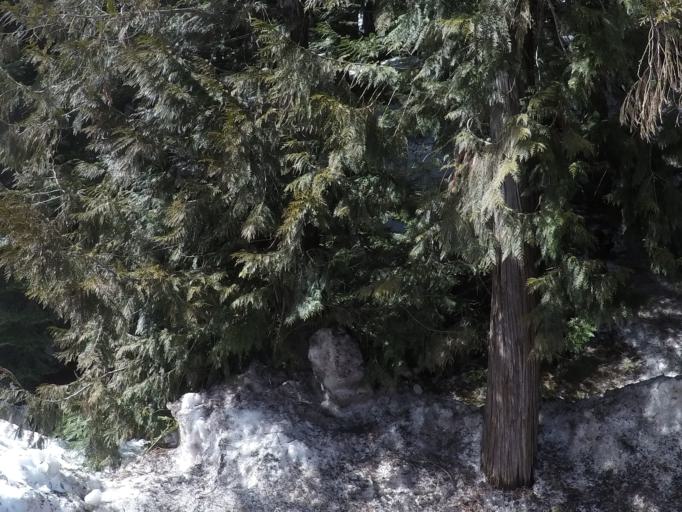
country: US
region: Montana
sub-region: Mineral County
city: Superior
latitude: 46.4755
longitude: -114.8852
